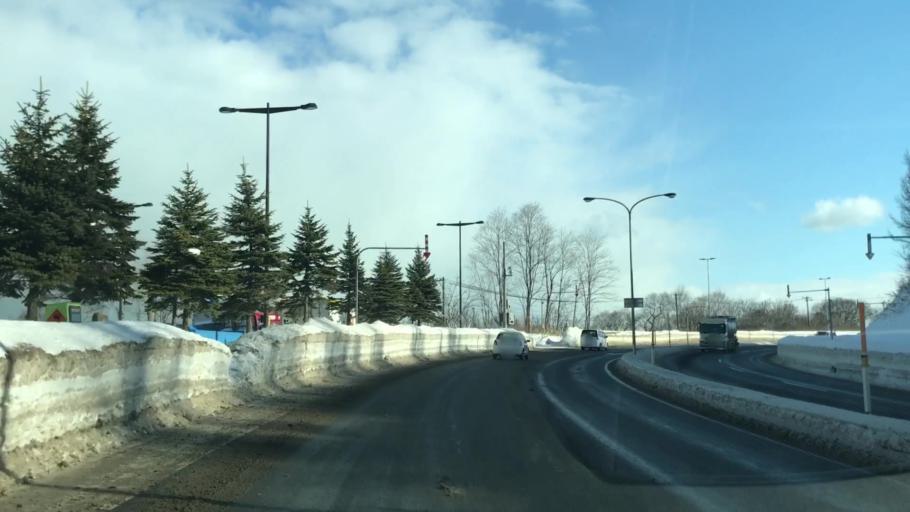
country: JP
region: Hokkaido
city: Otaru
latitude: 43.1750
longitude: 141.0663
